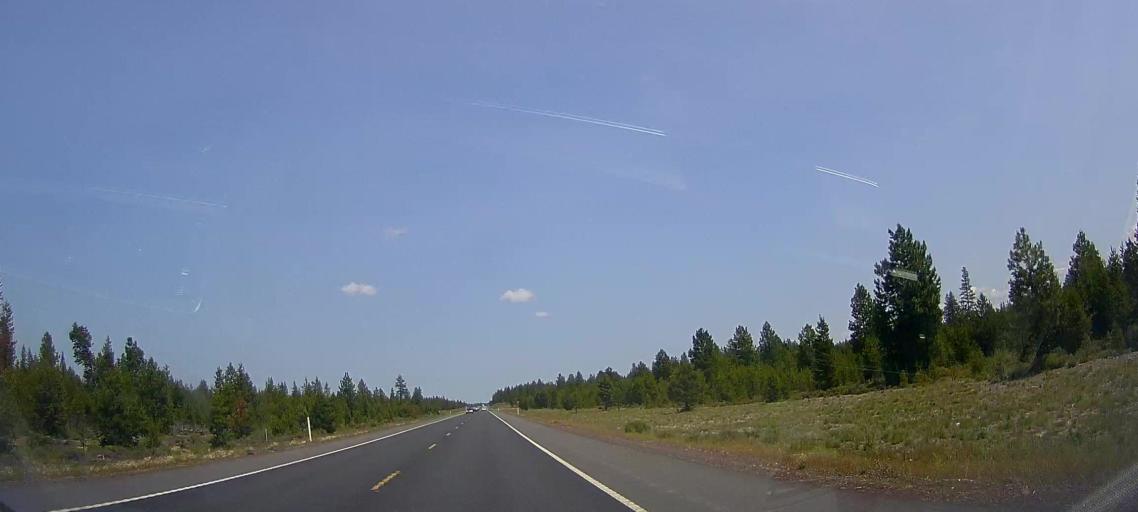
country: US
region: Oregon
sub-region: Deschutes County
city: La Pine
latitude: 43.5039
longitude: -121.6652
